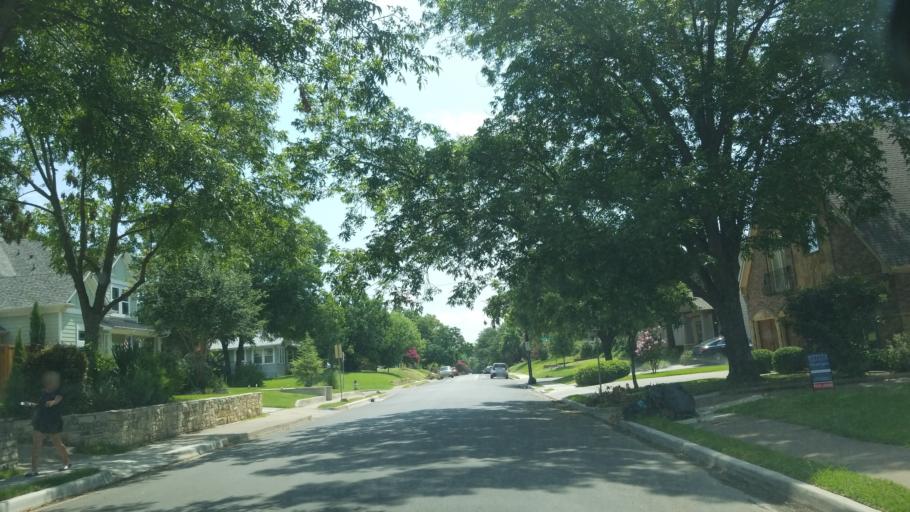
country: US
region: Texas
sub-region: Dallas County
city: Highland Park
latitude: 32.8148
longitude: -96.7665
